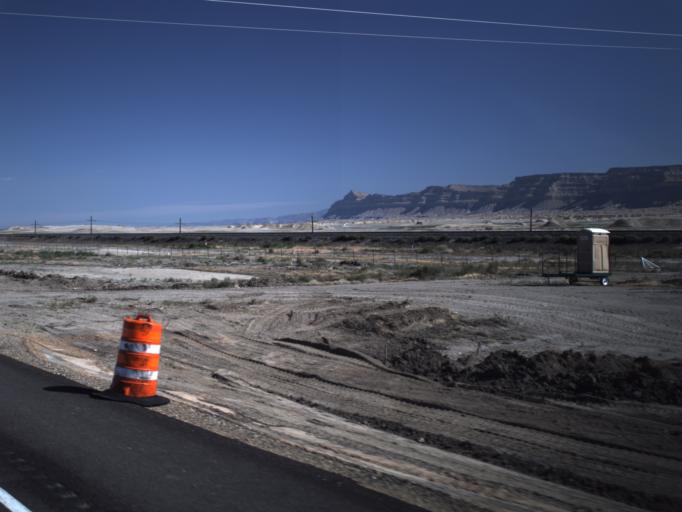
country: US
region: Utah
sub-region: Carbon County
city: East Carbon City
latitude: 39.0256
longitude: -110.2994
